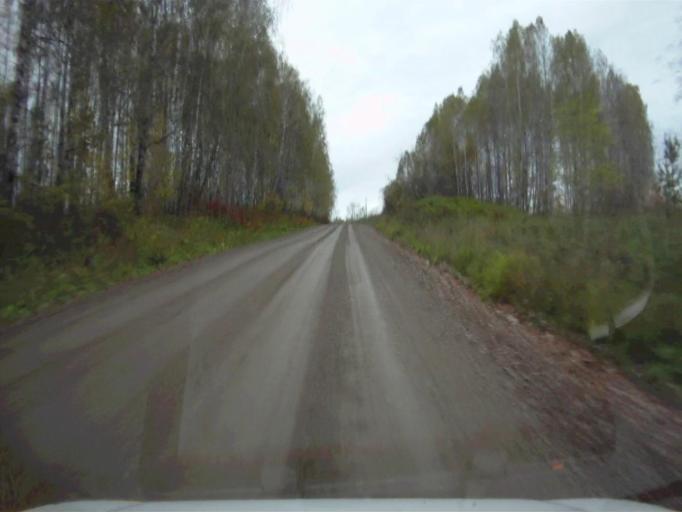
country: RU
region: Chelyabinsk
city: Nyazepetrovsk
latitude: 56.1342
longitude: 59.3095
